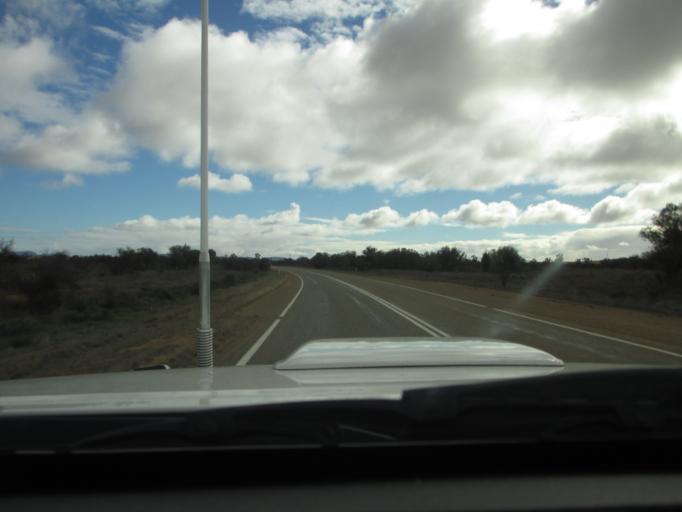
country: AU
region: South Australia
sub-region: Flinders Ranges
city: Quorn
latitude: -32.0792
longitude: 138.5028
